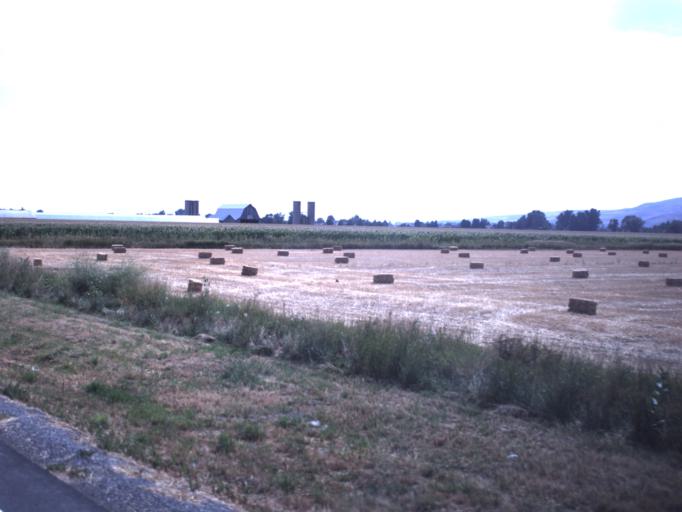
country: US
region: Utah
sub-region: Box Elder County
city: Garland
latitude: 41.8007
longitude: -112.1158
